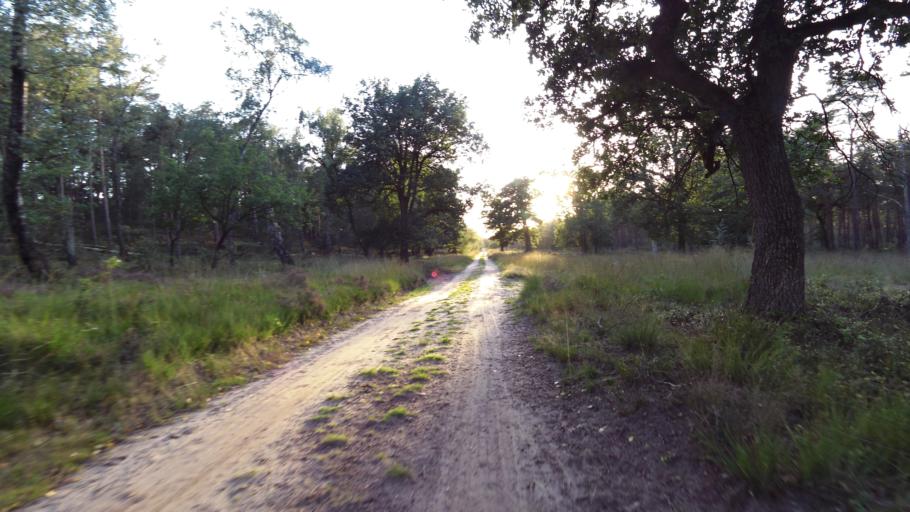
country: NL
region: Gelderland
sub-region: Gemeente Epe
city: Vaassen
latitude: 52.2714
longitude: 5.8900
